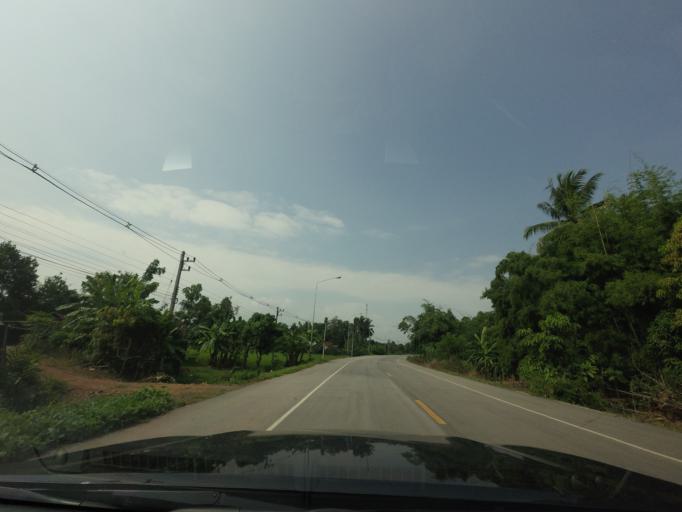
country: LA
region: Xiagnabouli
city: Muang Kenthao
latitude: 17.7078
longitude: 101.4229
